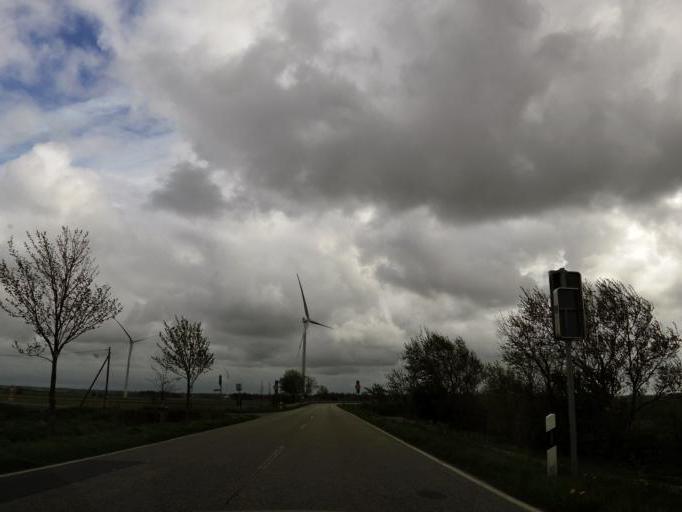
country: DE
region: Schleswig-Holstein
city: Suderlugum
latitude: 54.8992
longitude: 8.9117
